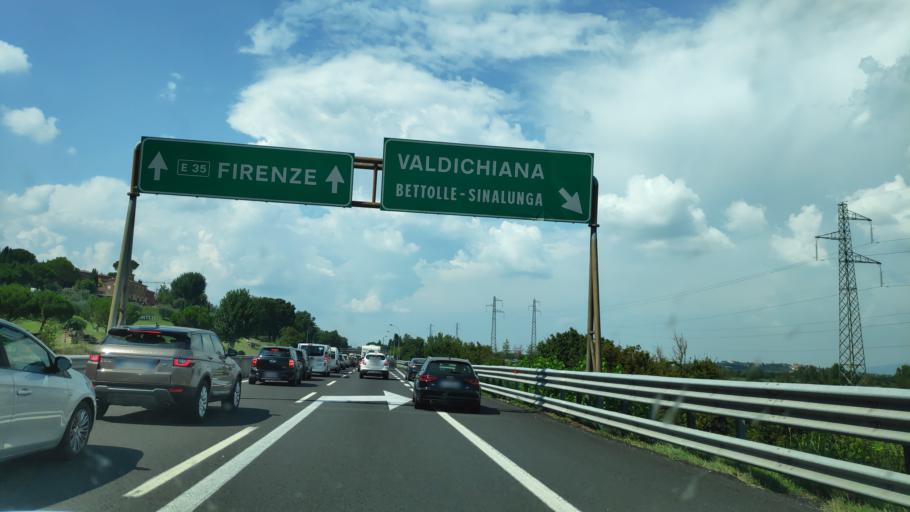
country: IT
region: Tuscany
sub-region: Provincia di Siena
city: Bettolle
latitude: 43.2083
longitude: 11.8116
